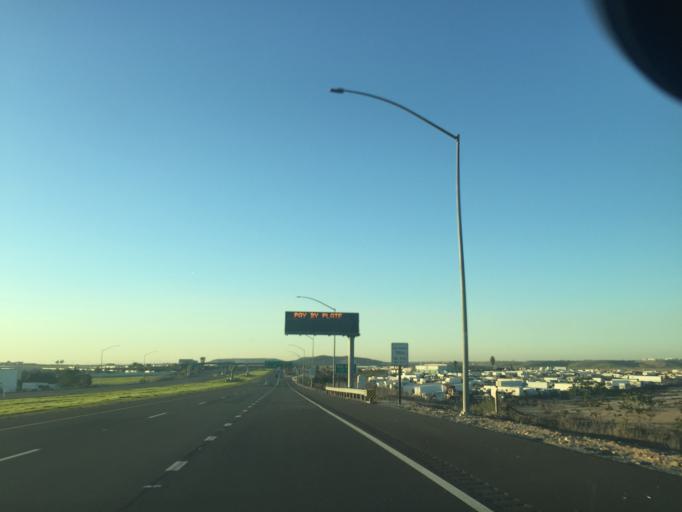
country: MX
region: Baja California
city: Tijuana
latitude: 32.5738
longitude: -116.9524
